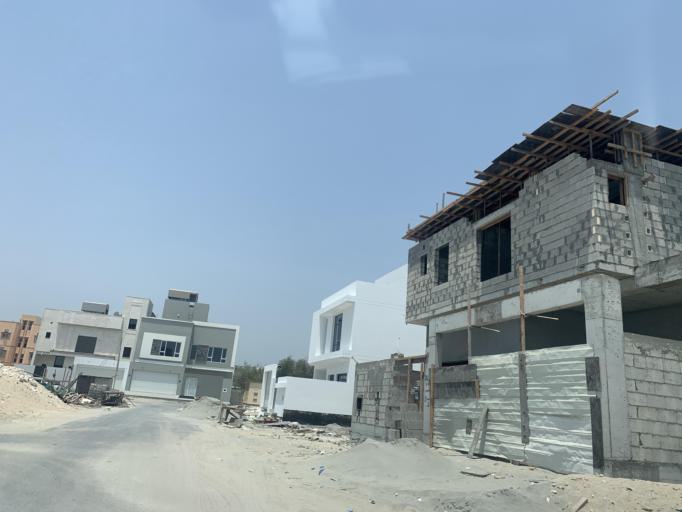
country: BH
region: Manama
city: Jidd Hafs
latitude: 26.2133
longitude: 50.4687
